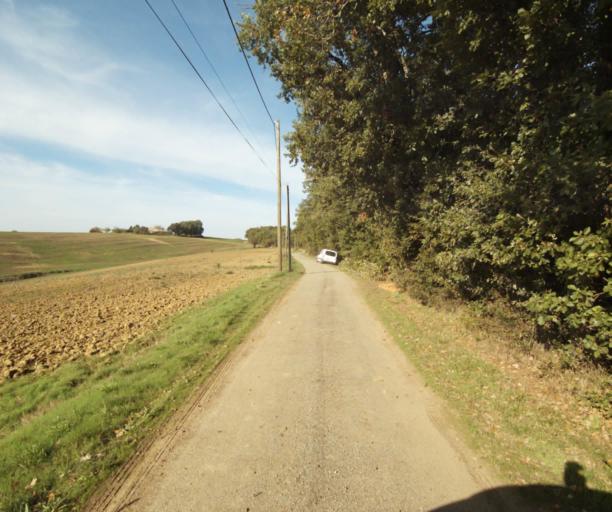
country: FR
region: Midi-Pyrenees
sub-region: Departement du Tarn-et-Garonne
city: Nohic
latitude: 43.9259
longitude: 1.4715
